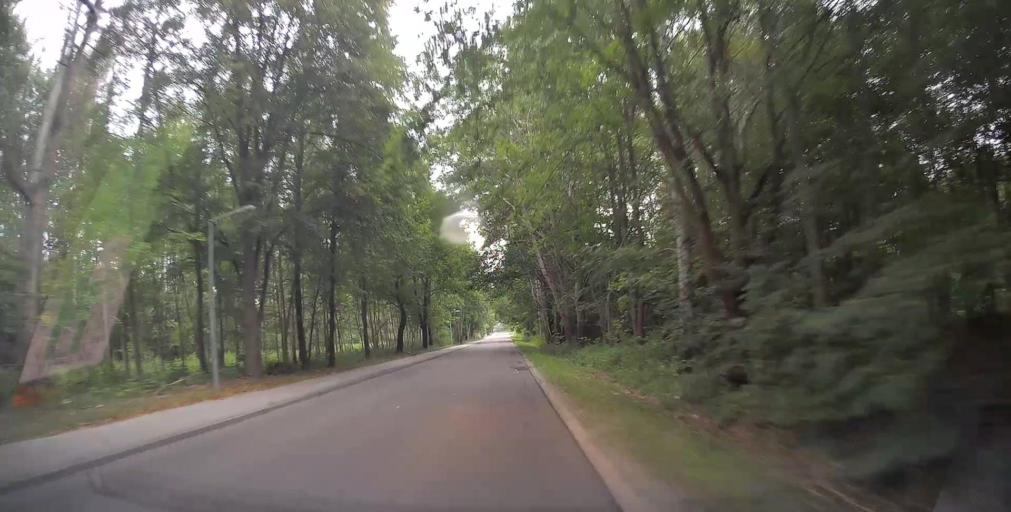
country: PL
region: Masovian Voivodeship
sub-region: Powiat bialobrzeski
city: Bialobrzegi
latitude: 51.6367
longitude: 20.9538
